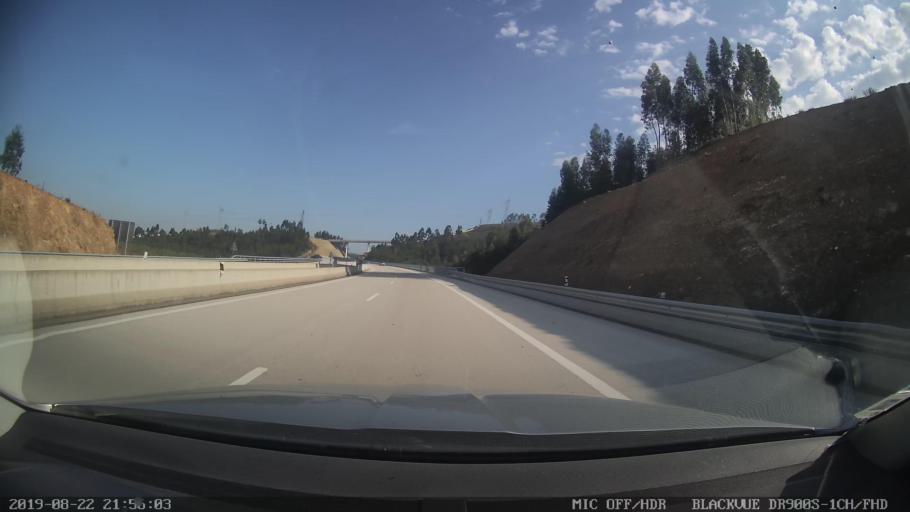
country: PT
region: Coimbra
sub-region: Coimbra
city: Coimbra
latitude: 40.1637
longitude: -8.3779
